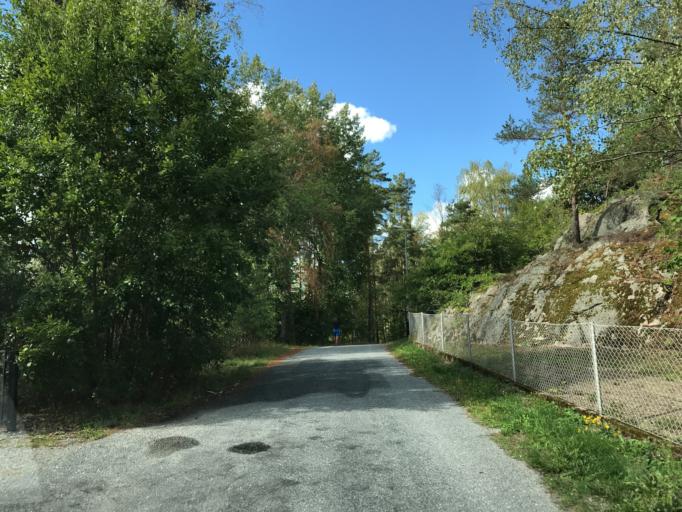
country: SE
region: Stockholm
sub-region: Sollentuna Kommun
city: Sollentuna
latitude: 59.4590
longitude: 17.9445
